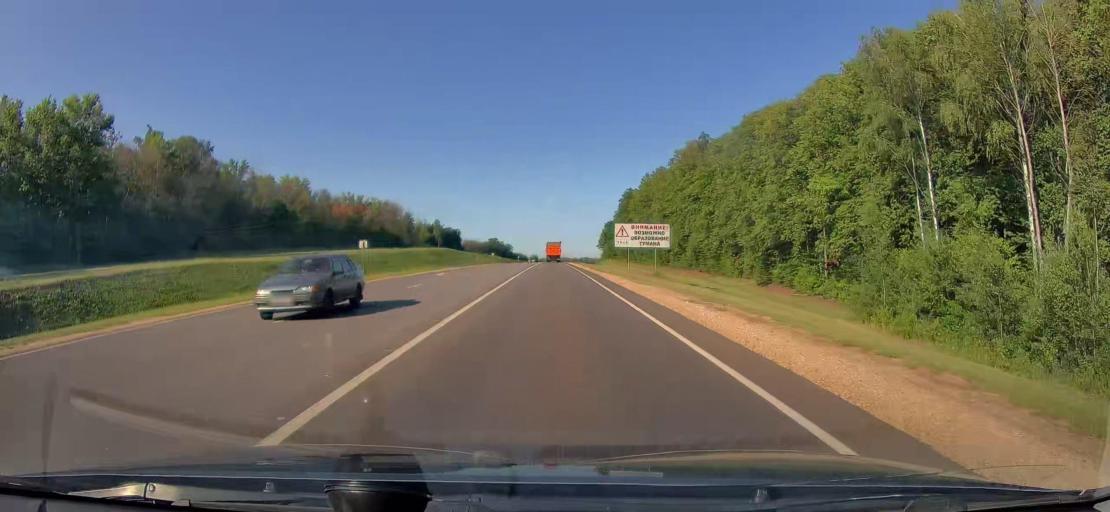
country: RU
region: Orjol
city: Orel
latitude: 53.1237
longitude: 36.3238
